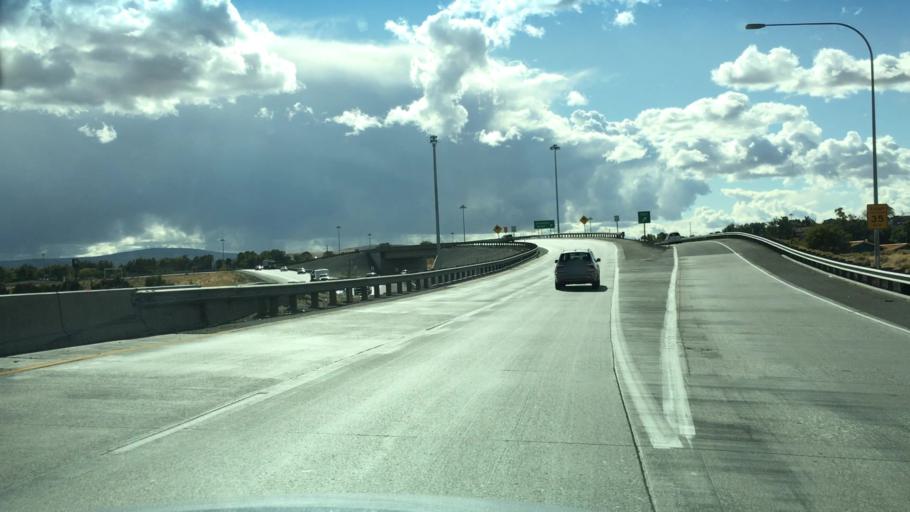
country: US
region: Washington
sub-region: Benton County
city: Kennewick
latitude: 46.2209
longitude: -119.1376
